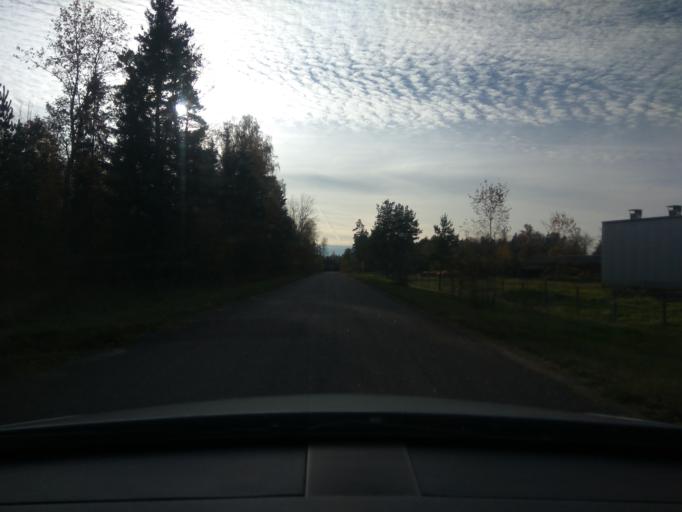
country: LV
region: Kuldigas Rajons
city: Kuldiga
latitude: 56.9161
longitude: 21.8970
